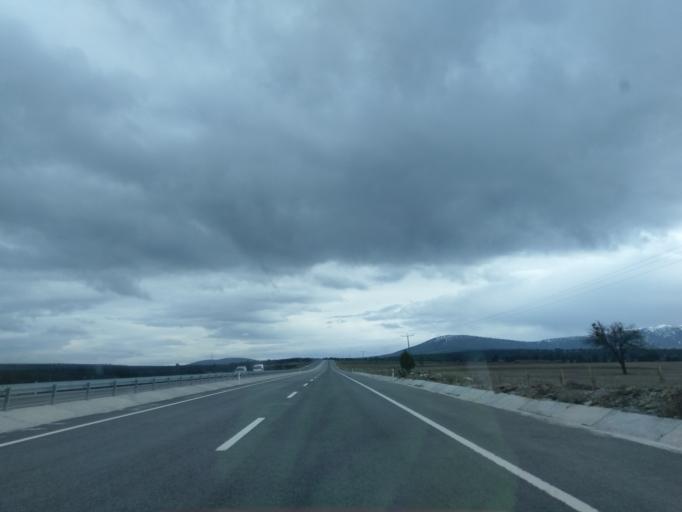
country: TR
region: Kuetahya
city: Cavdarhisar
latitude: 39.2257
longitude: 29.7197
